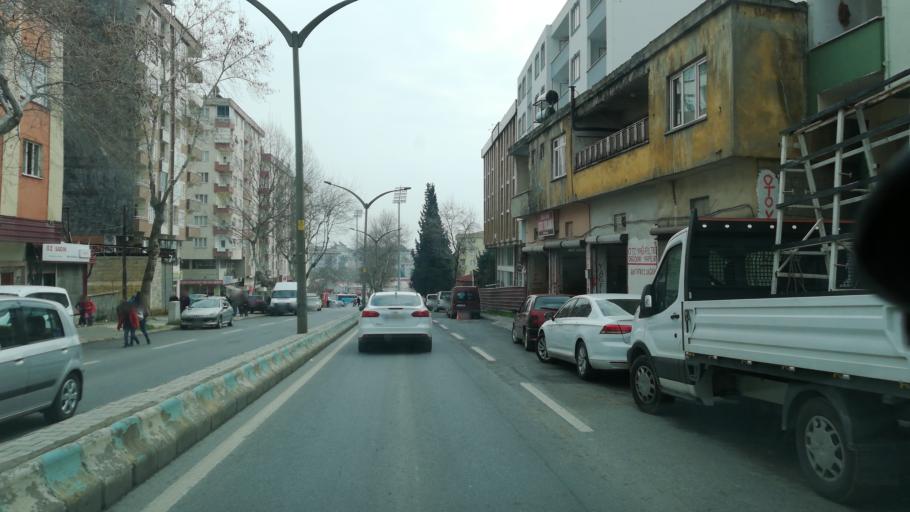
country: TR
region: Kahramanmaras
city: Kahramanmaras
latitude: 37.5764
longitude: 36.9202
